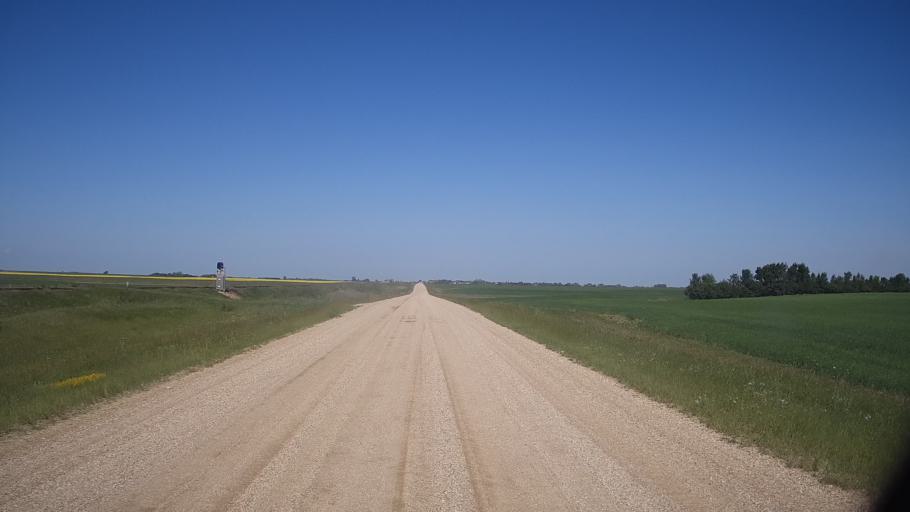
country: CA
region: Saskatchewan
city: Watrous
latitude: 51.8761
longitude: -106.0080
